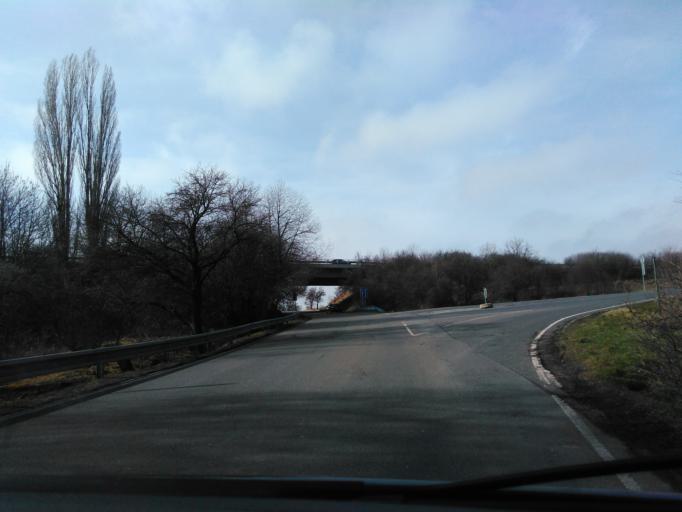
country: CZ
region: Central Bohemia
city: Tuchomerice
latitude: 50.1249
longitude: 14.2713
